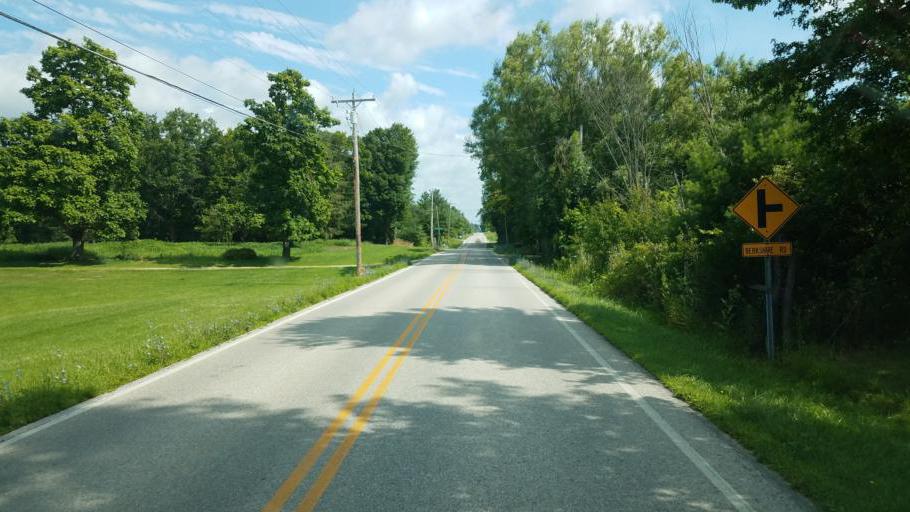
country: US
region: Ohio
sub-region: Delaware County
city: Sunbury
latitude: 40.2839
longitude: -82.9356
